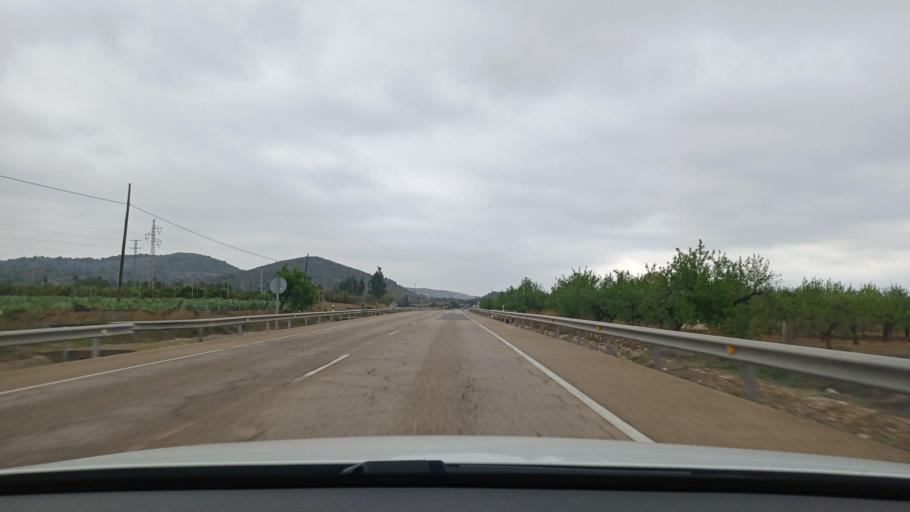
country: ES
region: Valencia
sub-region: Provincia de Castello
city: Torreblanca
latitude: 40.2069
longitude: 0.1807
